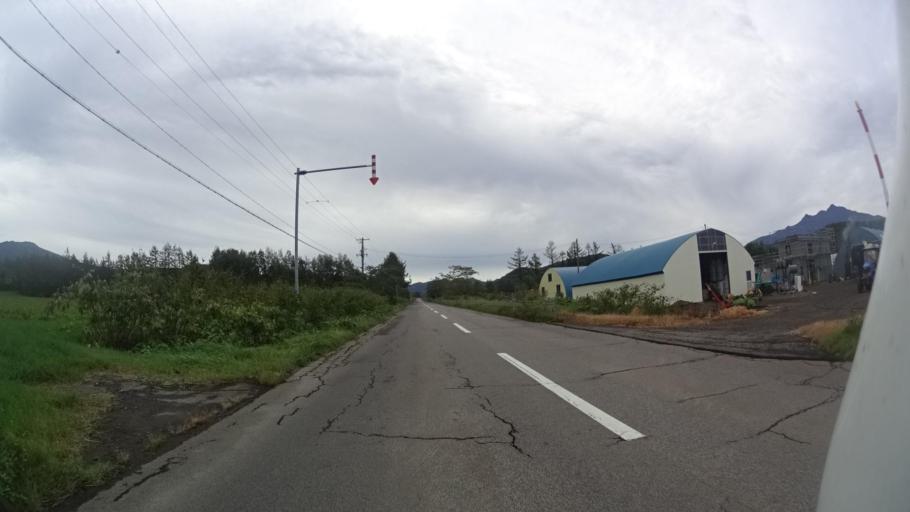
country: JP
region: Hokkaido
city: Shibetsu
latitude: 43.8602
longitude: 144.7616
